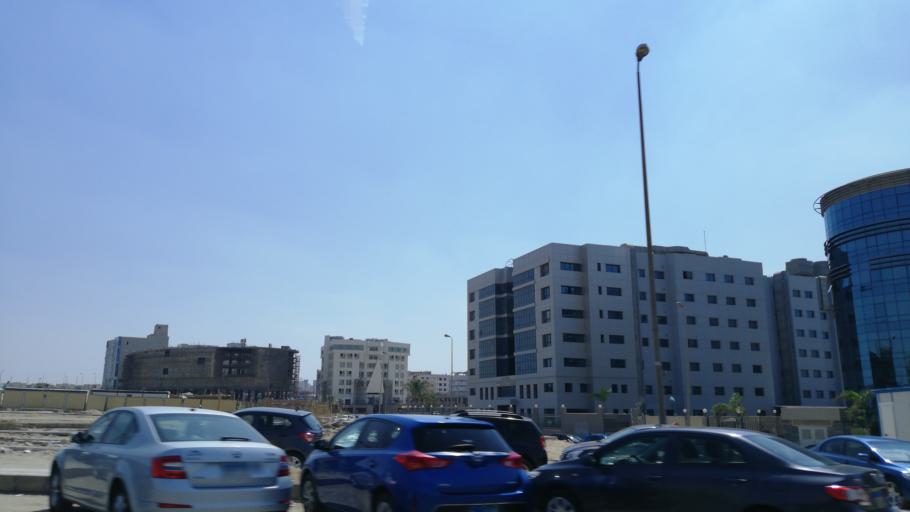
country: EG
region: Muhafazat al Qalyubiyah
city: Al Khankah
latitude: 30.0298
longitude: 31.4679
